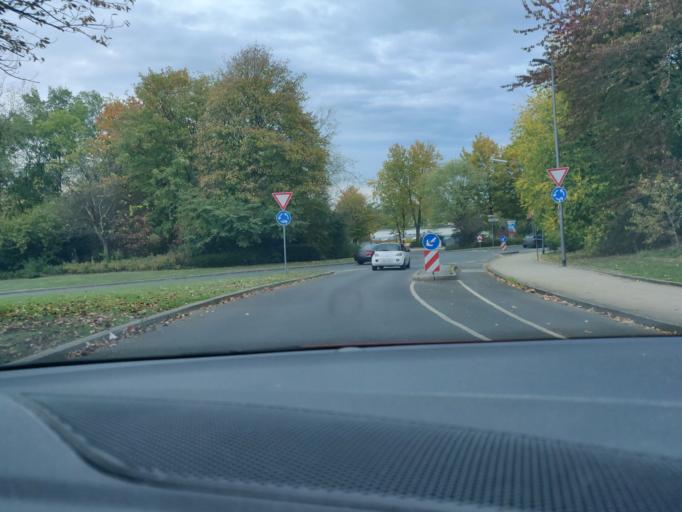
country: DE
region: North Rhine-Westphalia
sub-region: Regierungsbezirk Dusseldorf
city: Velbert
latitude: 51.3376
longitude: 7.0210
